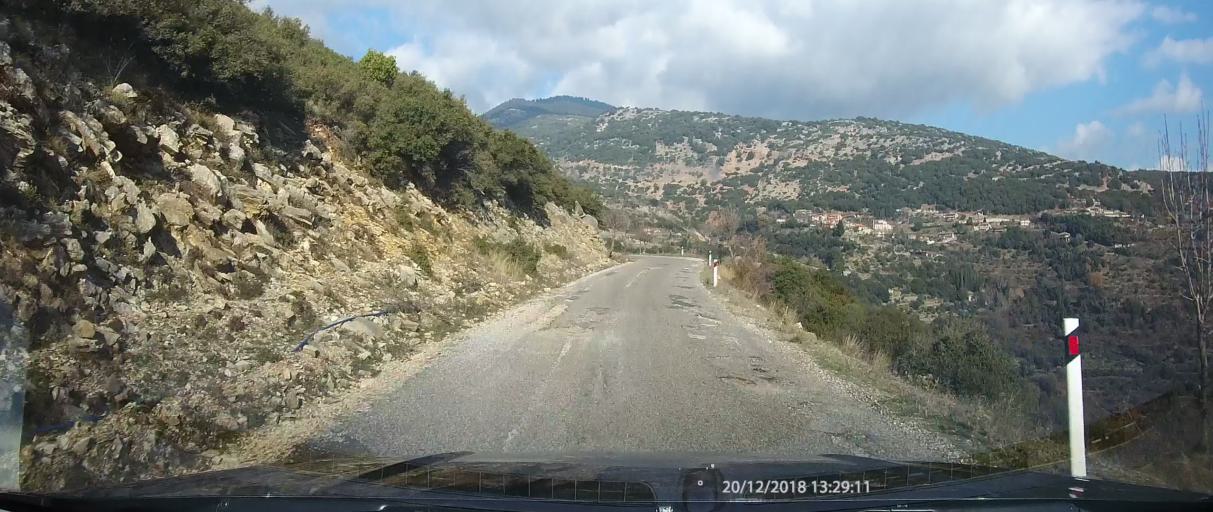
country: GR
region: West Greece
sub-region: Nomos Aitolias kai Akarnanias
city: Paravola
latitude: 38.6277
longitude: 21.5791
